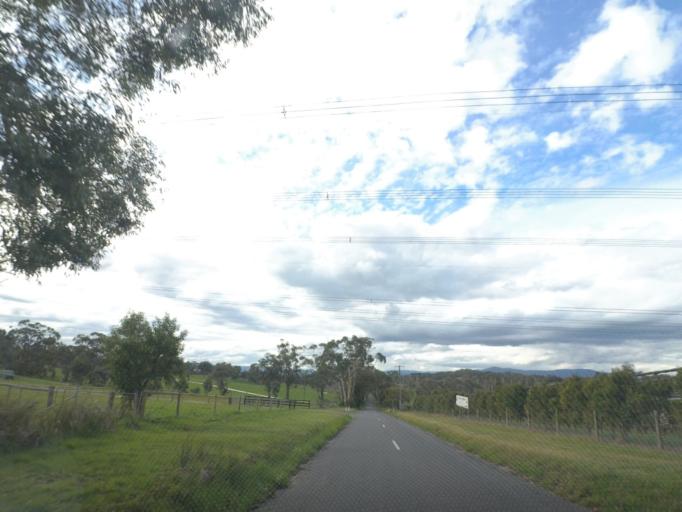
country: AU
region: Victoria
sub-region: Yarra Ranges
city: Mount Evelyn
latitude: -37.7479
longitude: 145.4116
